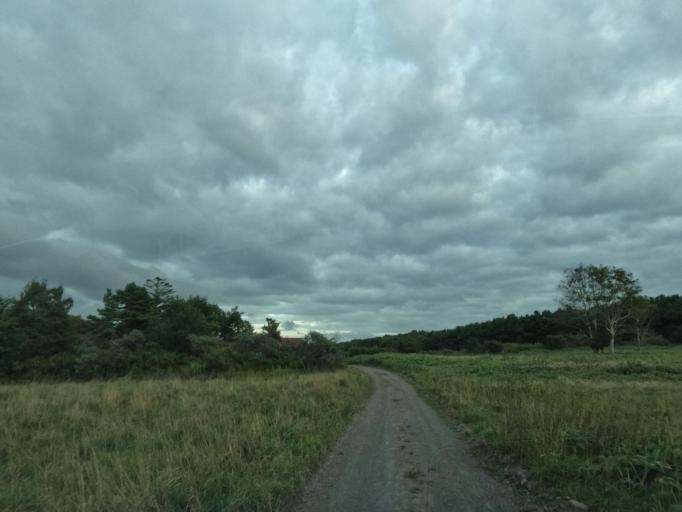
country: JP
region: Hokkaido
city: Muroran
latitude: 42.3713
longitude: 140.9702
